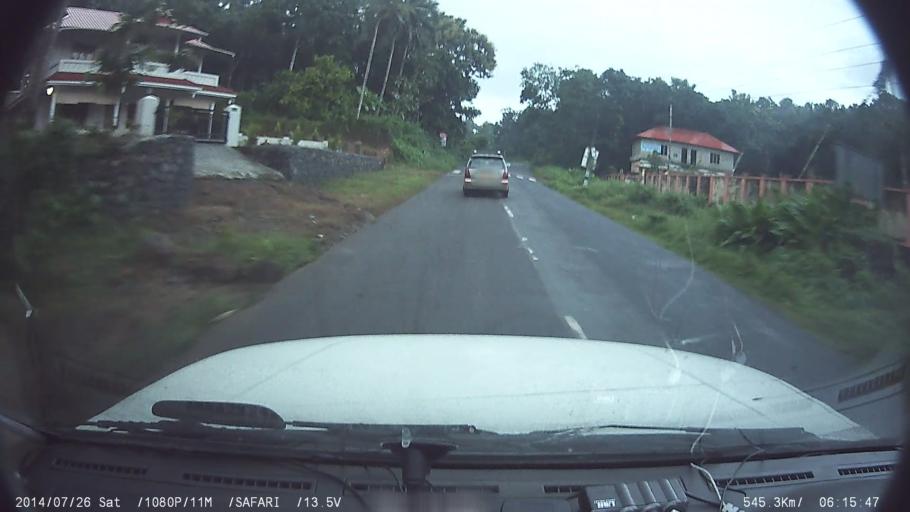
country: IN
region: Kerala
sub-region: Ernakulam
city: Piravam
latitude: 9.8371
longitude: 76.5918
